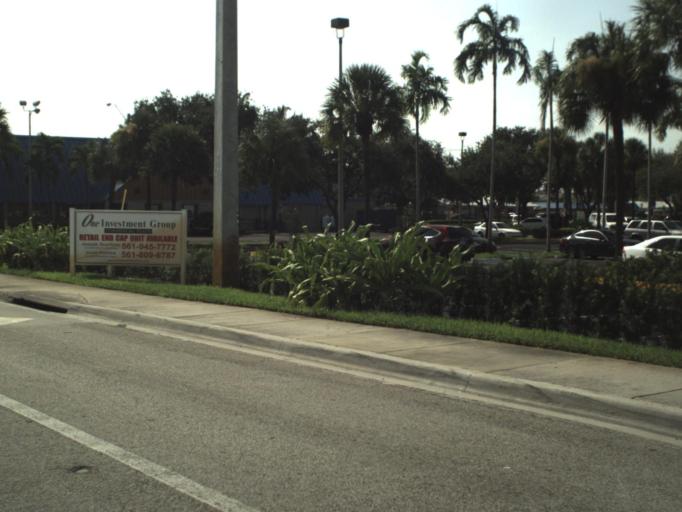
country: US
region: Florida
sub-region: Broward County
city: Tedder
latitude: 26.2750
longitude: -80.1348
